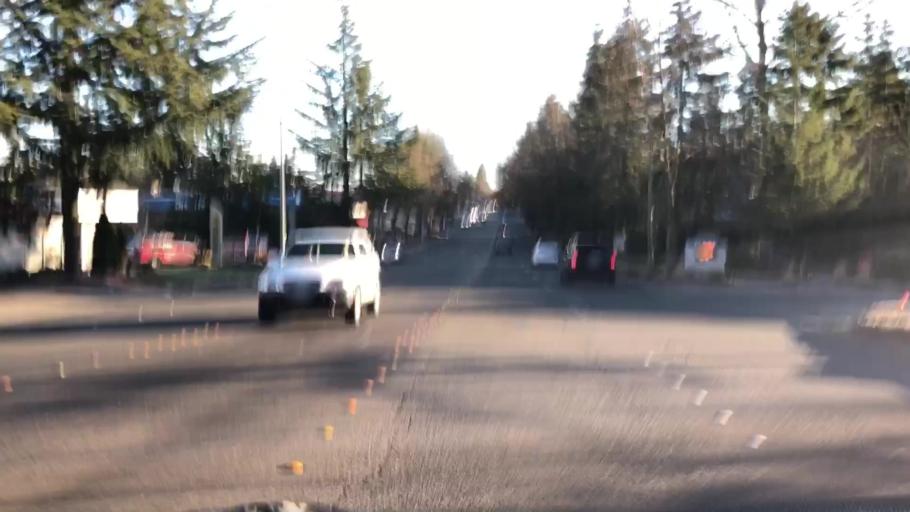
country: US
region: Washington
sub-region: King County
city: Bellevue
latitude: 47.6209
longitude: -122.1706
